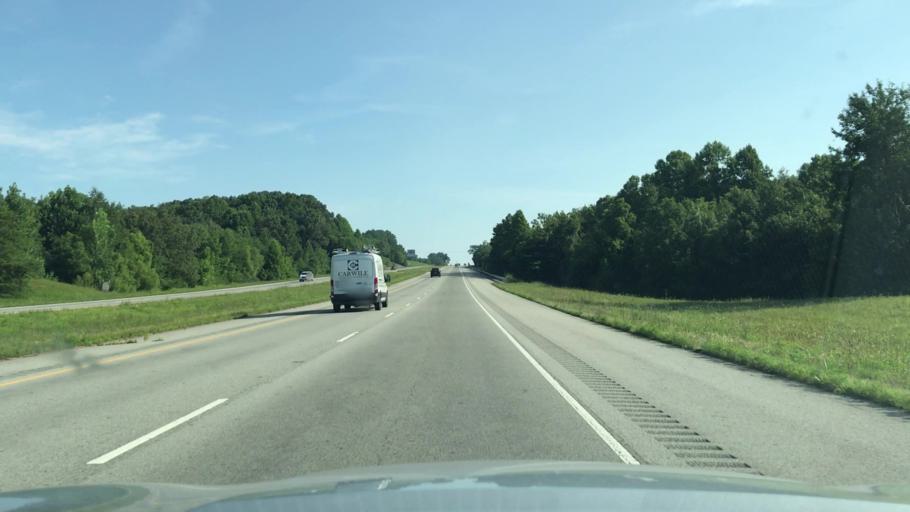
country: US
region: Tennessee
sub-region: Putnam County
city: Algood
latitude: 36.2593
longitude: -85.3922
